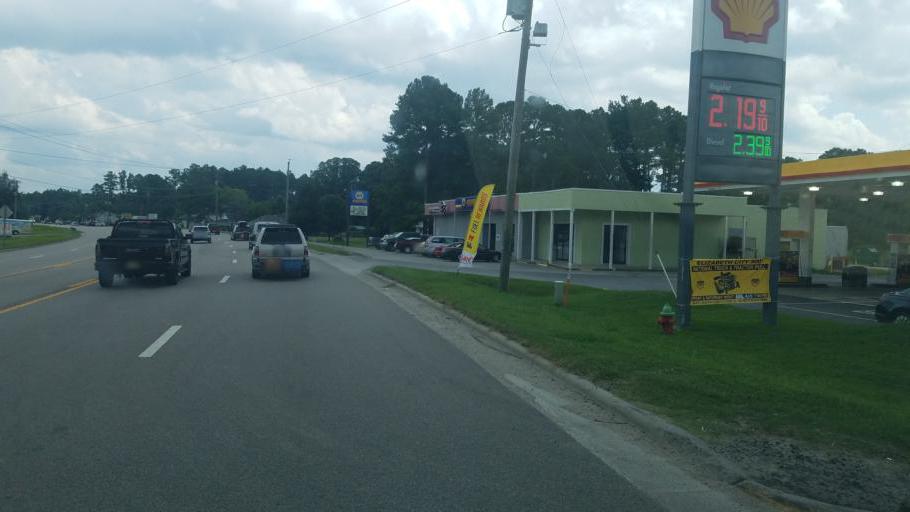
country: US
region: North Carolina
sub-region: Currituck County
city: Moyock
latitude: 36.5300
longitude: -76.1839
